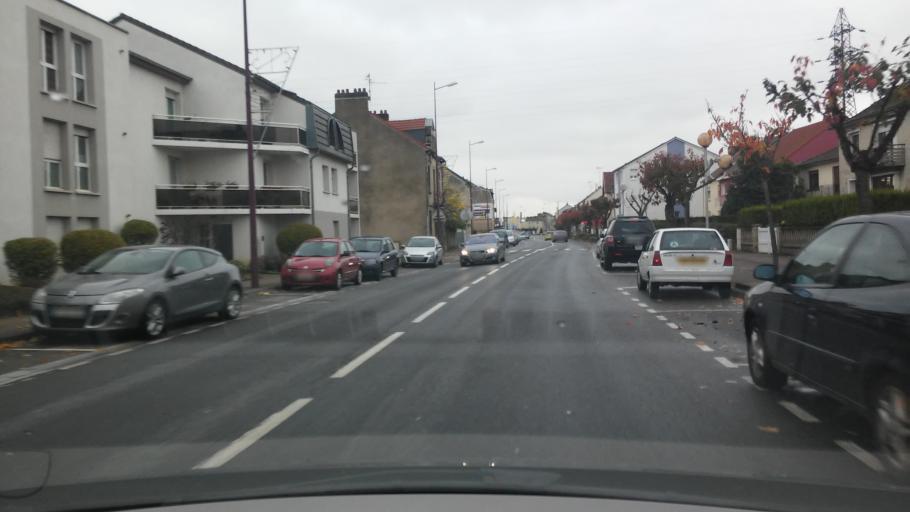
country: FR
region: Lorraine
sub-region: Departement de la Moselle
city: Talange
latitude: 49.2402
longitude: 6.1690
